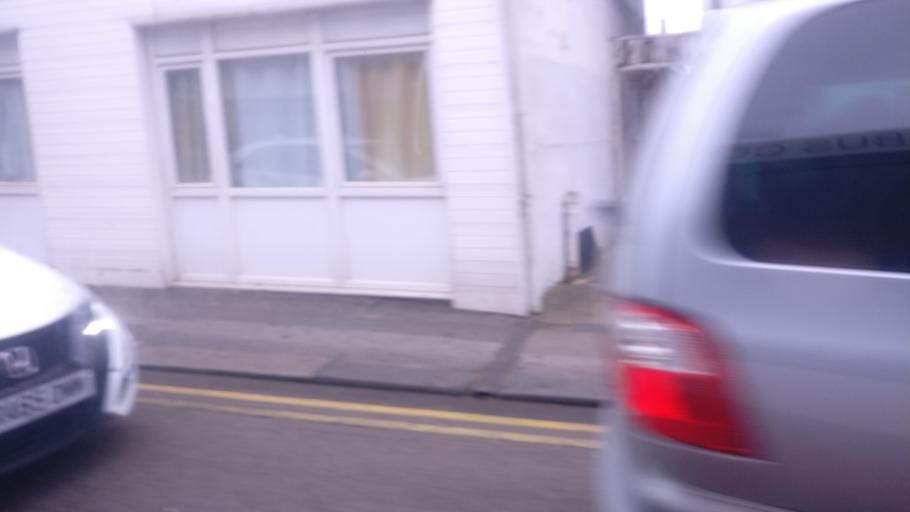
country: GB
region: England
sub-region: Surrey
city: Addlestone
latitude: 51.3709
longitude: -0.4928
